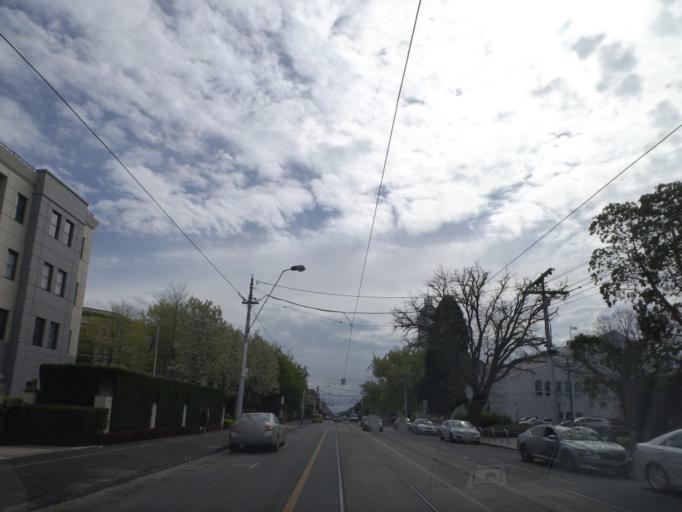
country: AU
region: Victoria
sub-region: Glen Eira
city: Caulfield North
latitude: -37.8568
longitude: 145.0308
